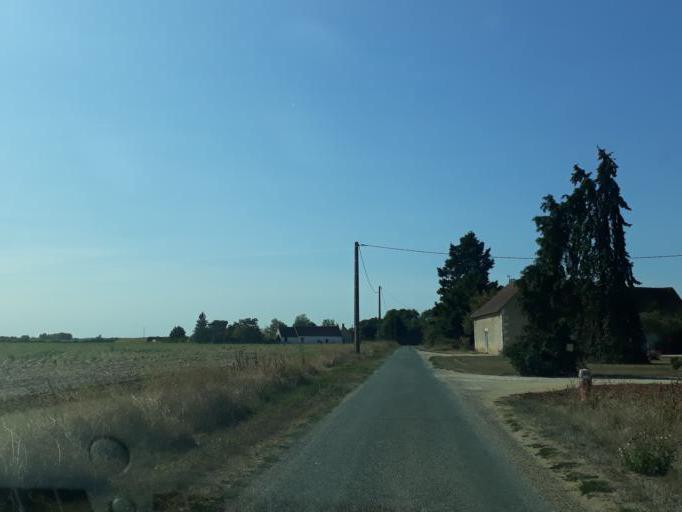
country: FR
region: Centre
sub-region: Departement de l'Indre
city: Chabris
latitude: 47.2661
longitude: 1.6160
